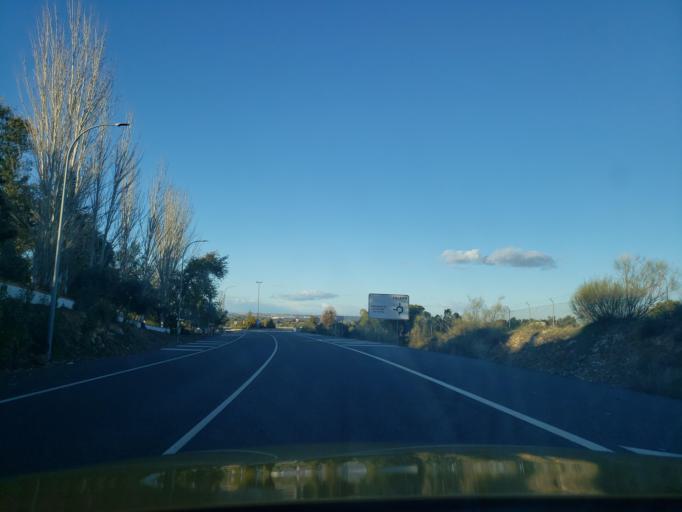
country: ES
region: Castille-La Mancha
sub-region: Province of Toledo
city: Cobisa
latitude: 39.8270
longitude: -4.0179
